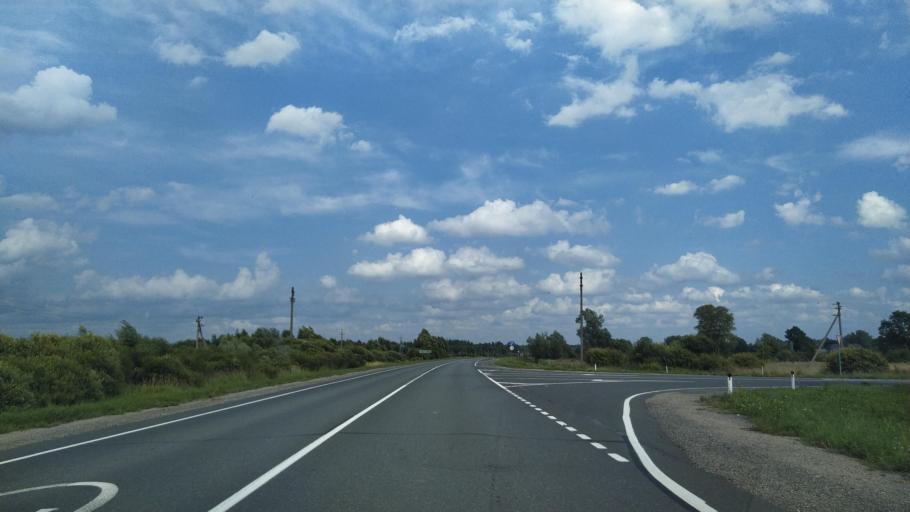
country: RU
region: Pskov
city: Dno
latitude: 57.9827
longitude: 29.7540
